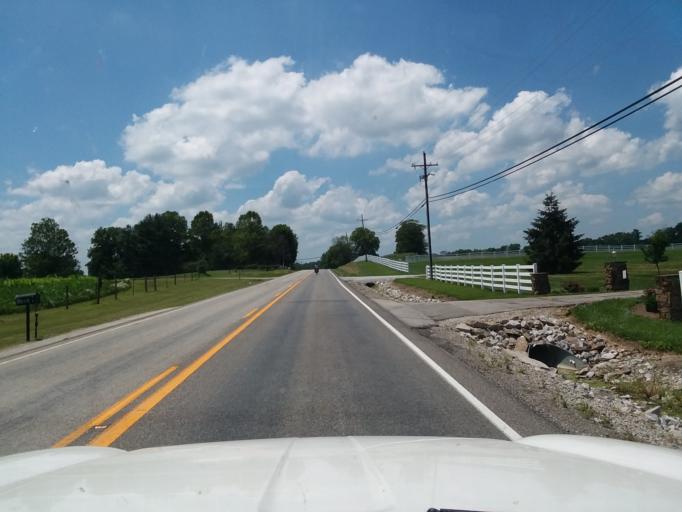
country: US
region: Indiana
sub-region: Johnson County
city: Trafalgar
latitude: 39.3714
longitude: -86.2719
